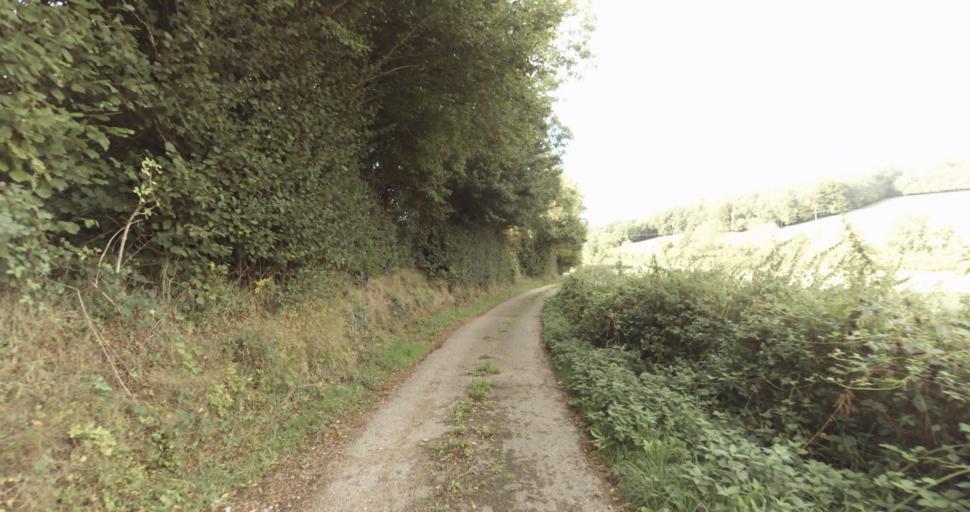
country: FR
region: Lower Normandy
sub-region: Departement de l'Orne
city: Gace
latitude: 48.8307
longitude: 0.2235
